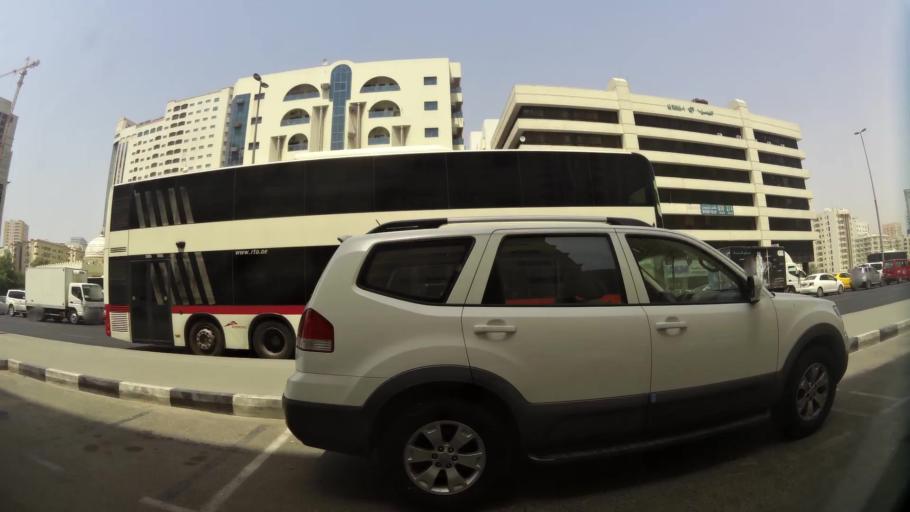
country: AE
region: Ash Shariqah
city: Sharjah
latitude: 25.3382
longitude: 55.3890
